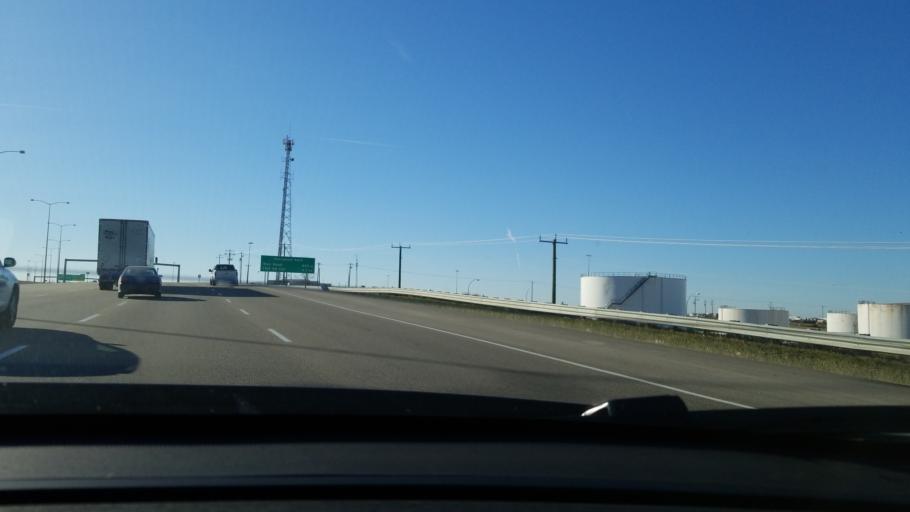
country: CA
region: Alberta
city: Sherwood Park
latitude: 53.5291
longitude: -113.3450
